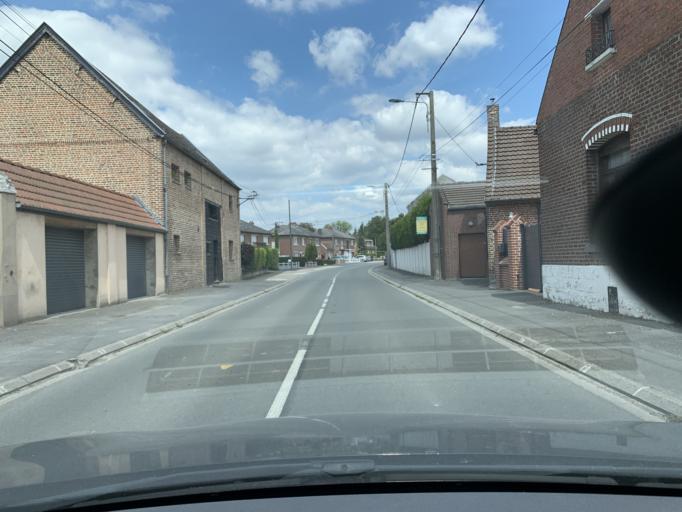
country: FR
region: Nord-Pas-de-Calais
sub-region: Departement du Nord
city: Arleux
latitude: 50.2823
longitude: 3.1047
